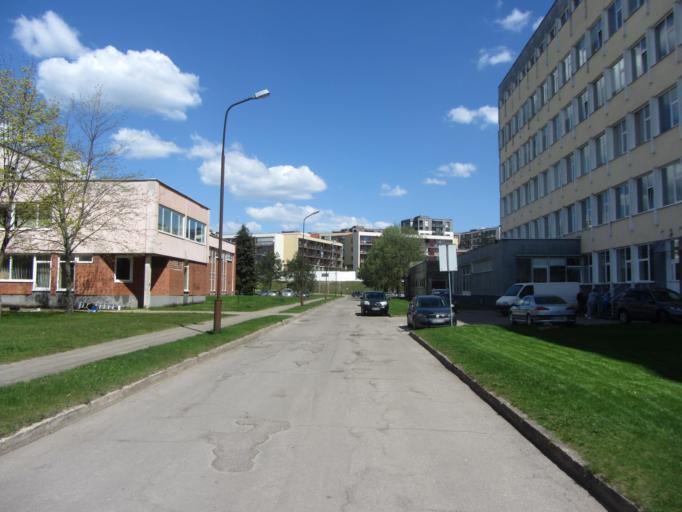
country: LT
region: Vilnius County
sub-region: Vilnius
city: Fabijoniskes
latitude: 54.7528
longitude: 25.2623
